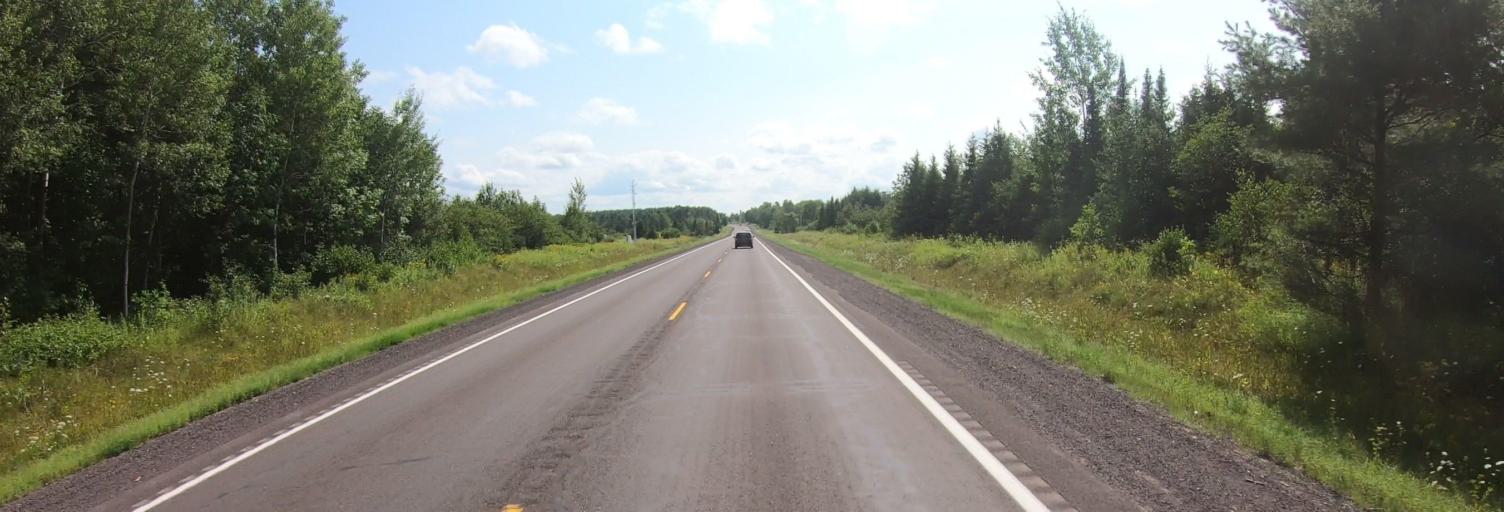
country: US
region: Michigan
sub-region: Ontonagon County
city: Ontonagon
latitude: 46.7240
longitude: -89.1524
